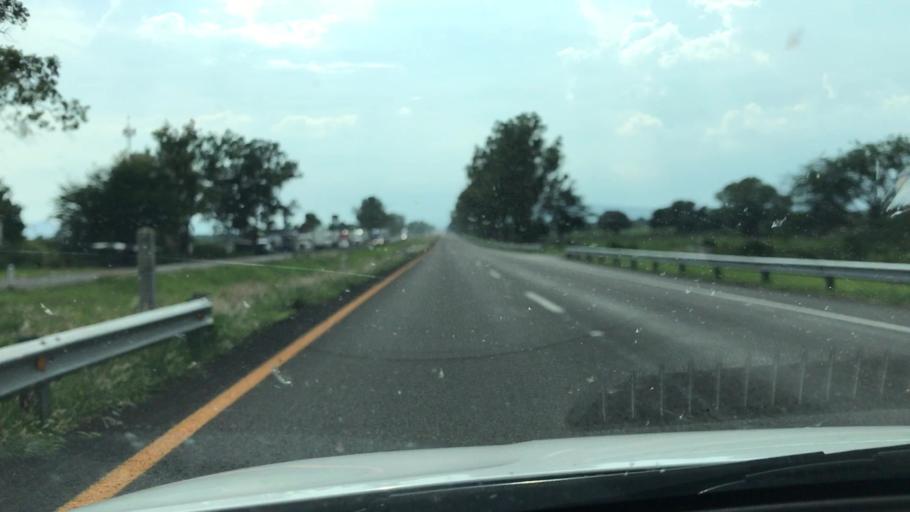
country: MX
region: Jalisco
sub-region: Ocotlan
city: Joconoxtle (La Tuna)
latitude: 20.3742
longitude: -102.6632
